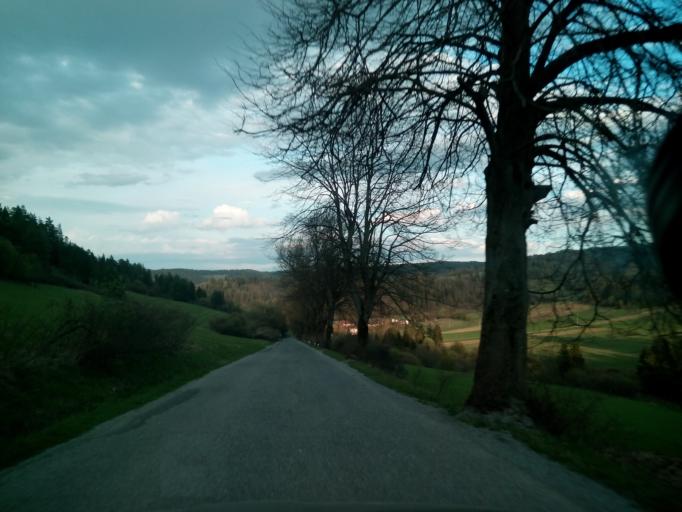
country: PL
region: Lesser Poland Voivodeship
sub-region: Powiat nowotarski
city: Niedzica
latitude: 49.3347
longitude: 20.3315
